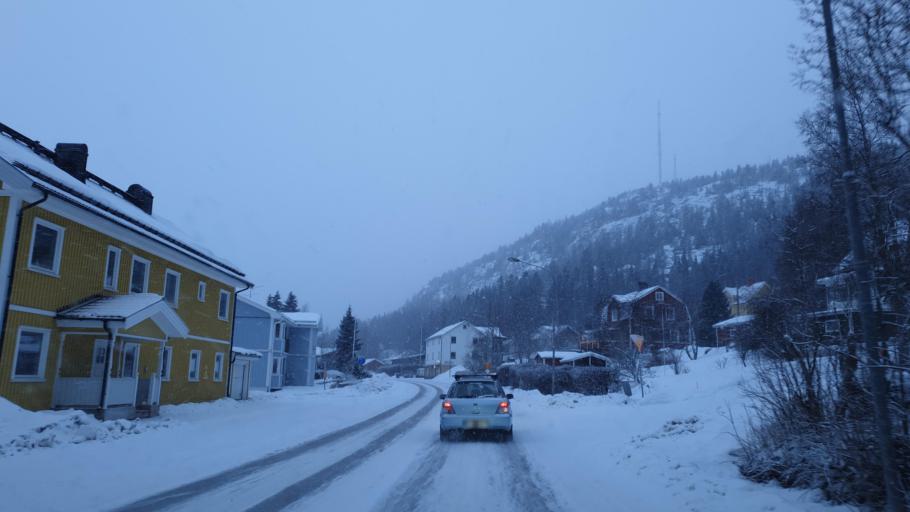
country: SE
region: Vaesternorrland
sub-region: OErnskoeldsviks Kommun
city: Ornskoldsvik
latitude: 63.2978
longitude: 18.6745
